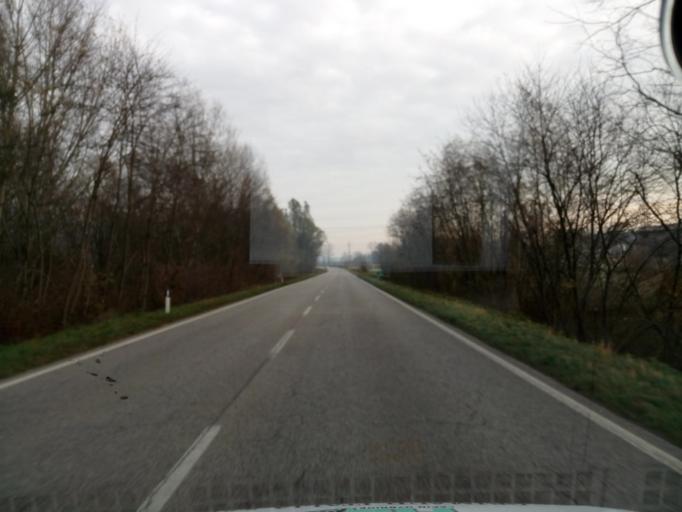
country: IT
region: Veneto
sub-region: Provincia di Treviso
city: Pederobba
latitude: 45.8596
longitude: 11.9377
